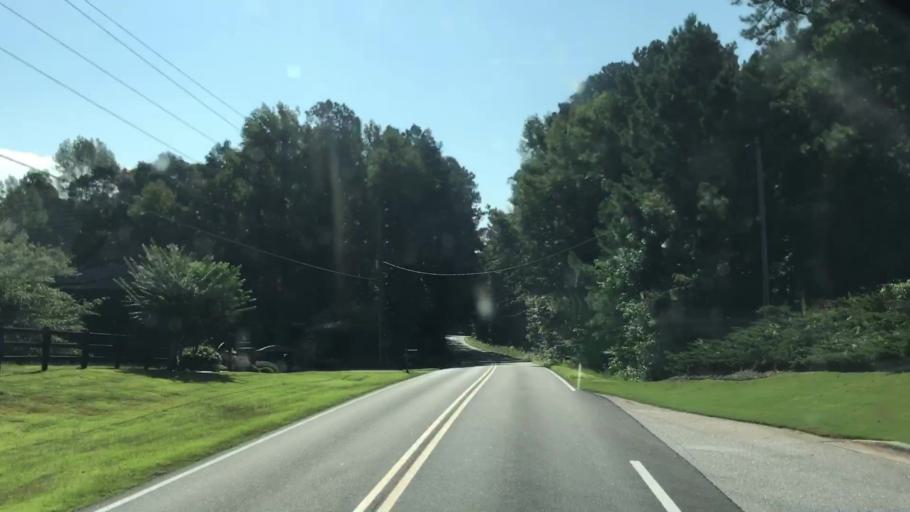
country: US
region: Georgia
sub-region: Walton County
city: Monroe
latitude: 33.8579
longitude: -83.7925
